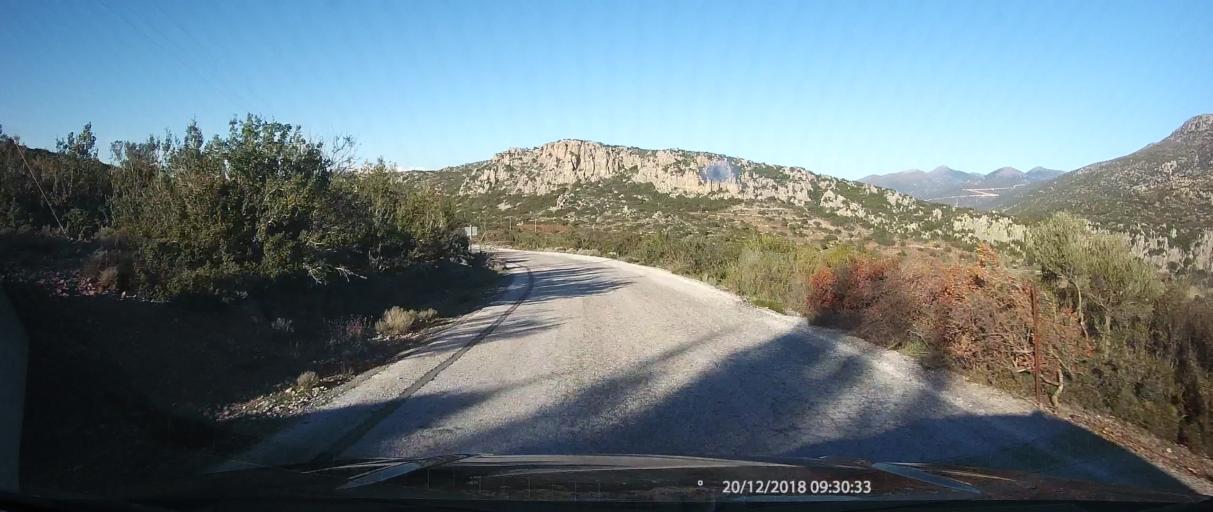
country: GR
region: Peloponnese
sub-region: Nomos Lakonias
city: Kato Glikovrisi
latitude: 36.9527
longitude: 22.8460
